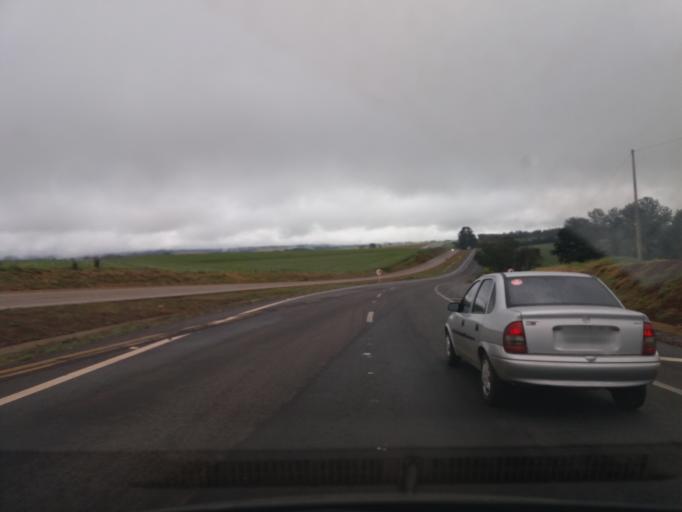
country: BR
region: Parana
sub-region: Cascavel
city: Cascavel
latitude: -25.1075
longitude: -53.5916
